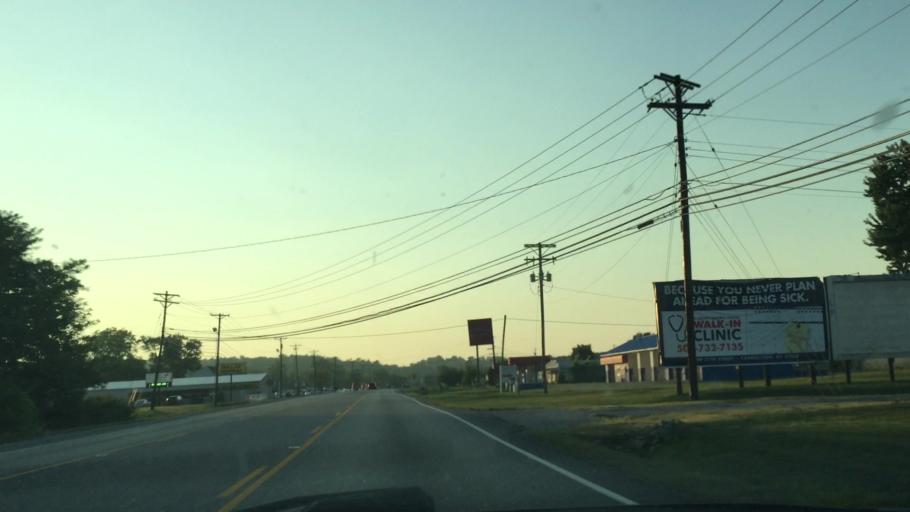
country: US
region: Kentucky
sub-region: Carroll County
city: Carrollton
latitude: 38.6605
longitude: -85.1382
